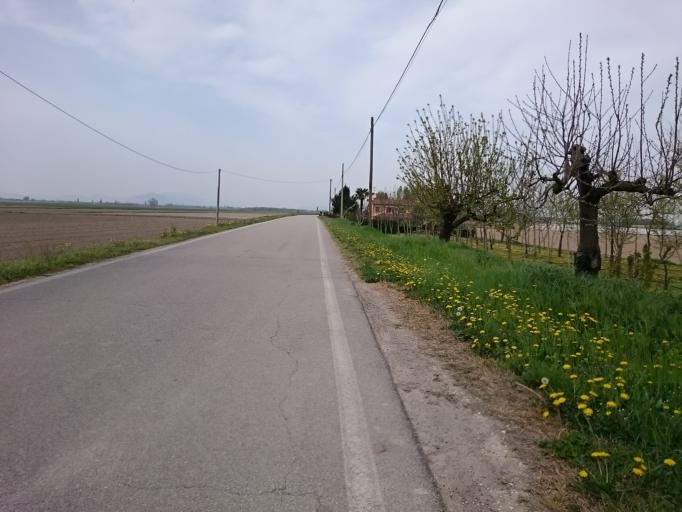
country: IT
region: Veneto
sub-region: Provincia di Padova
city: Anguillara Veneta
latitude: 45.1589
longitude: 11.8507
